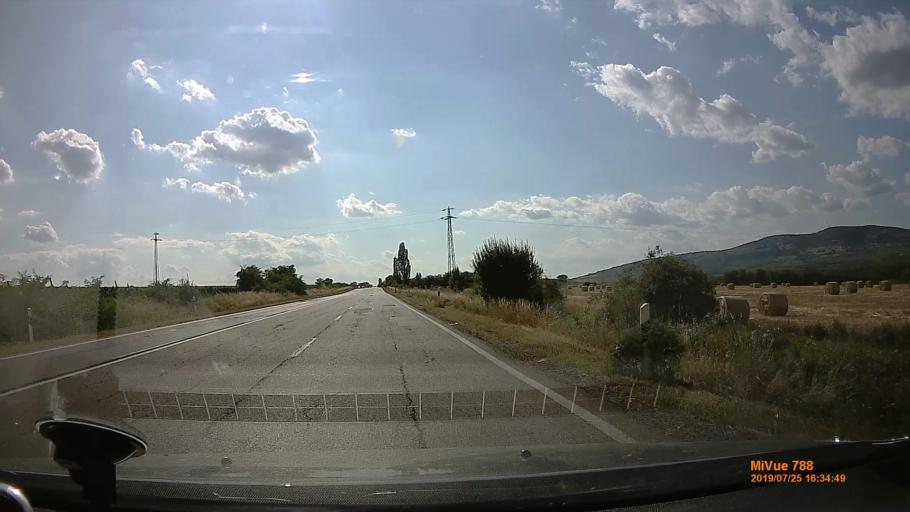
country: HU
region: Heves
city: Abasar
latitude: 47.7675
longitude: 20.0161
